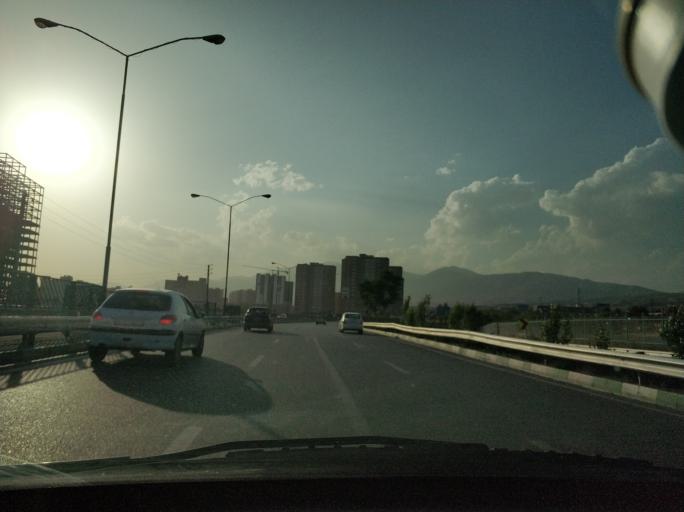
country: IR
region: Tehran
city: Tajrish
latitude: 35.7524
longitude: 51.5789
